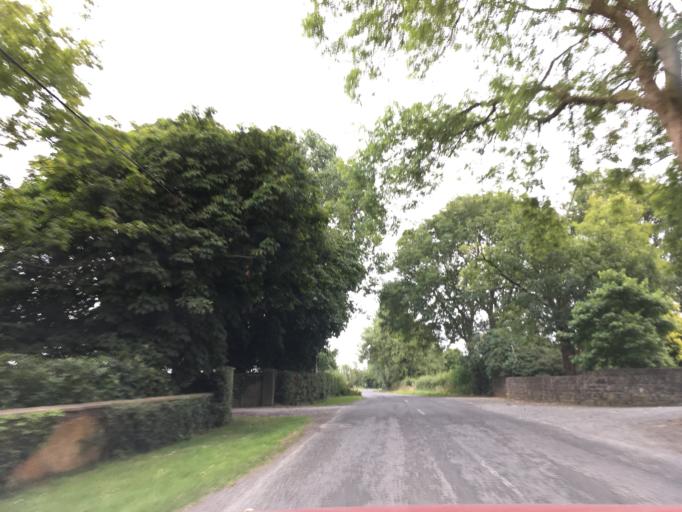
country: IE
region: Munster
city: Cashel
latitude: 52.4756
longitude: -7.8774
